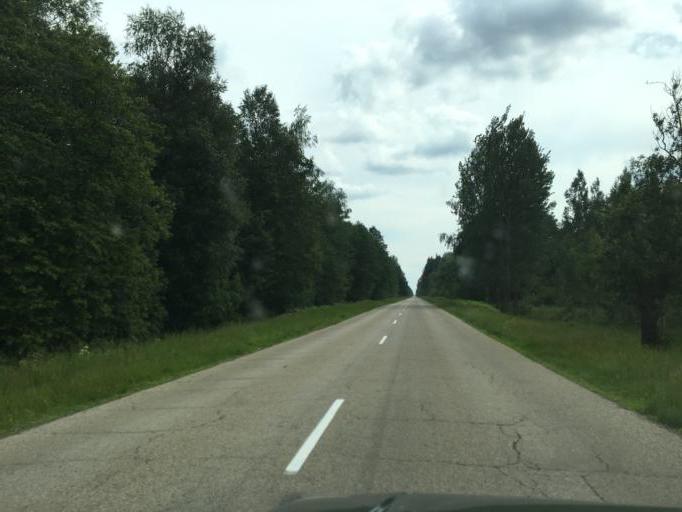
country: LV
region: Rugaju
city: Rugaji
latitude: 56.8033
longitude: 27.0973
